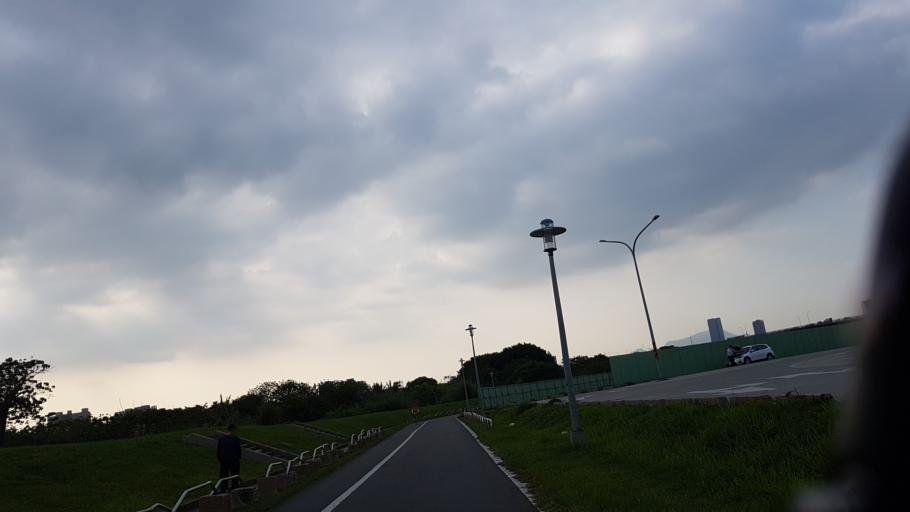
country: TW
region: Taipei
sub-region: Taipei
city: Banqiao
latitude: 25.0315
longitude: 121.4872
